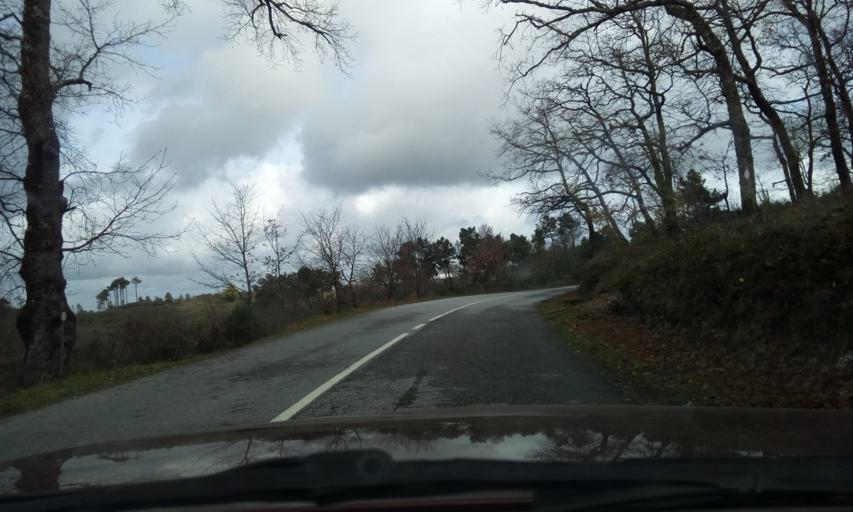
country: PT
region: Guarda
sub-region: Fornos de Algodres
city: Fornos de Algodres
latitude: 40.6350
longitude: -7.5485
